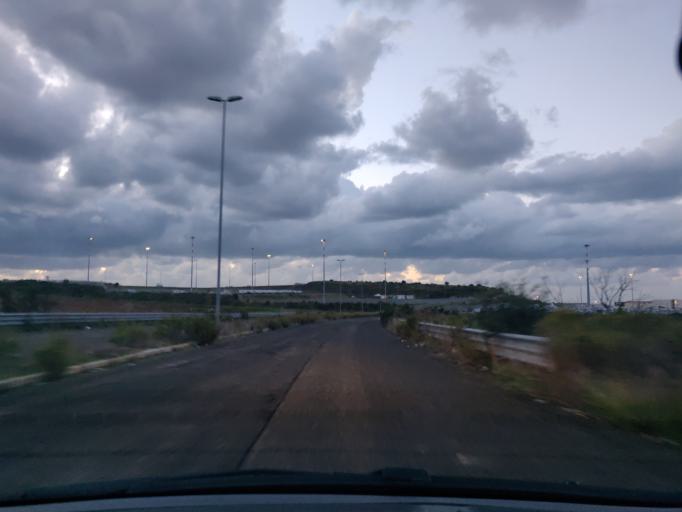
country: IT
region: Latium
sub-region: Citta metropolitana di Roma Capitale
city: Aurelia
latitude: 42.1309
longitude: 11.7772
